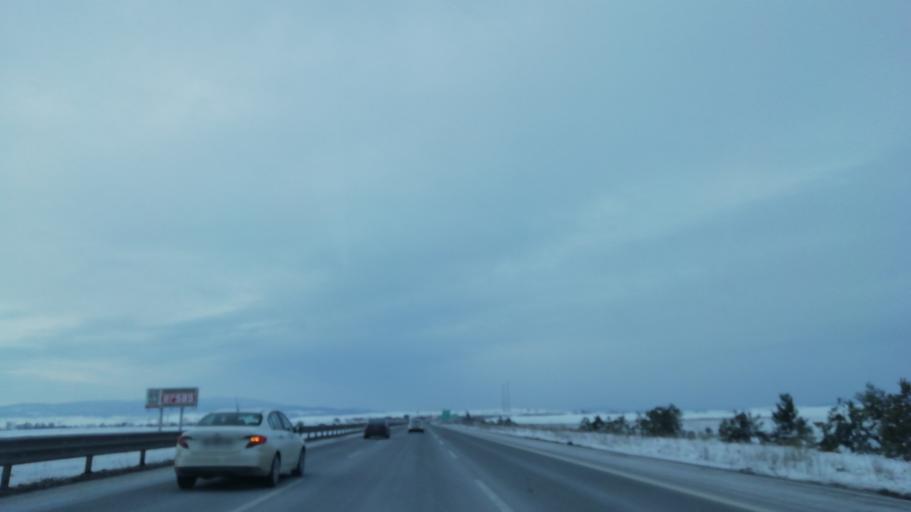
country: TR
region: Bolu
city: Dortdivan
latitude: 40.7467
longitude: 32.1000
